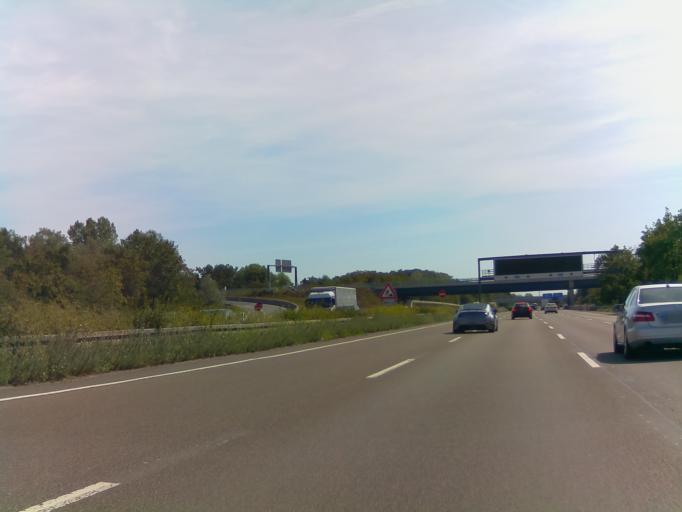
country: DE
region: Hesse
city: Griesheim
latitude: 49.8734
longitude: 8.6013
